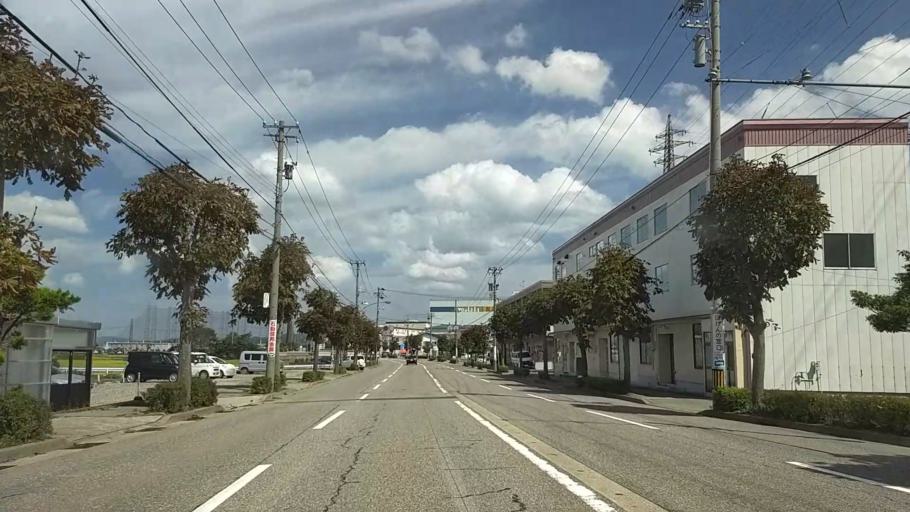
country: JP
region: Ishikawa
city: Kanazawa-shi
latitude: 36.5882
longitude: 136.6517
